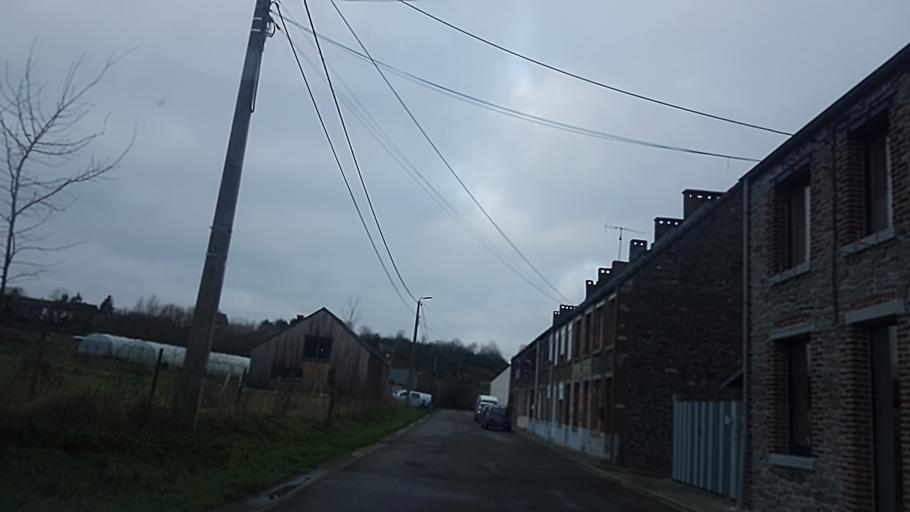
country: FR
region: Champagne-Ardenne
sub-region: Departement des Ardennes
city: Haybes
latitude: 50.0667
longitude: 4.6128
